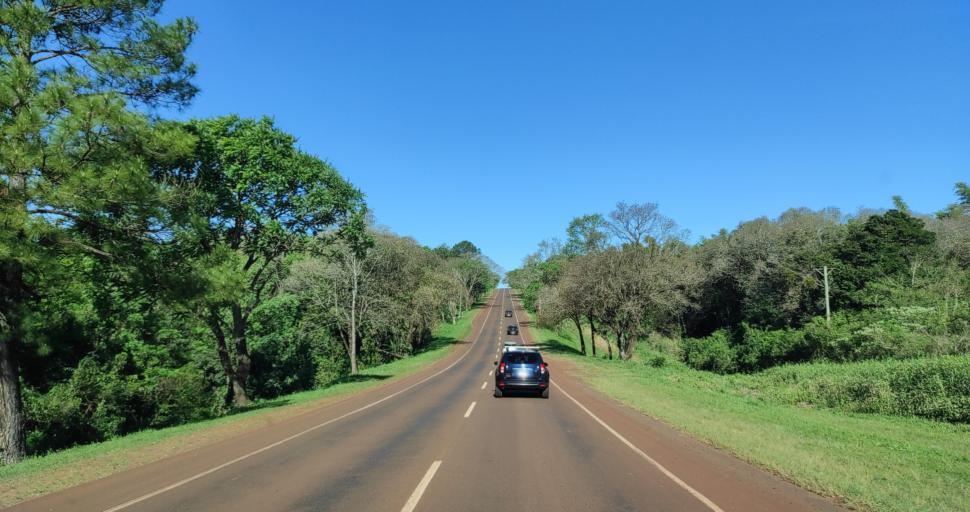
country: AR
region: Misiones
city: Guarani
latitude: -27.4896
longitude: -55.1767
